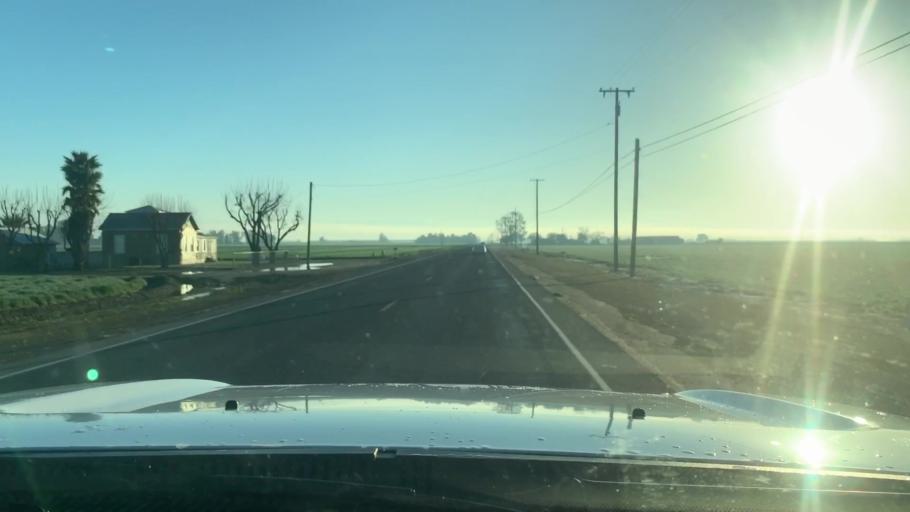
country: US
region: California
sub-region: Kings County
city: Home Garden
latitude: 36.2112
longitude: -119.6329
